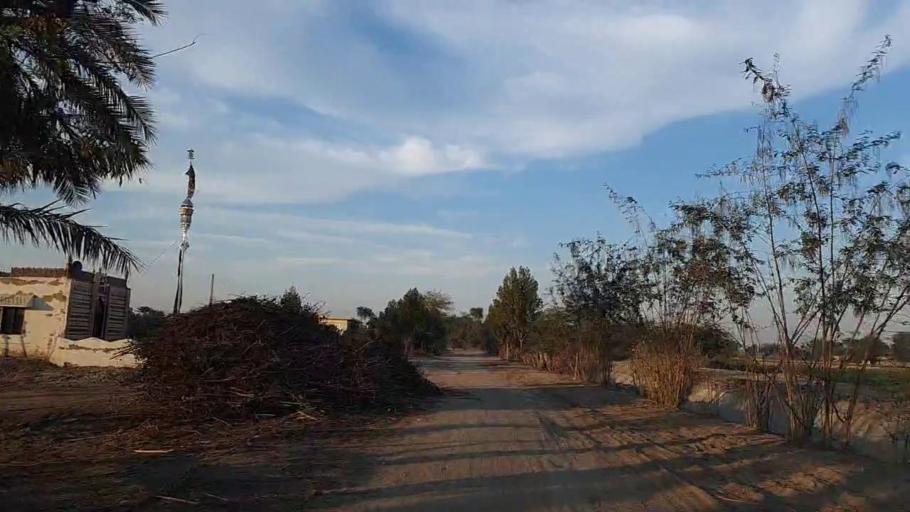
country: PK
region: Sindh
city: Bandhi
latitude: 26.6081
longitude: 68.3593
